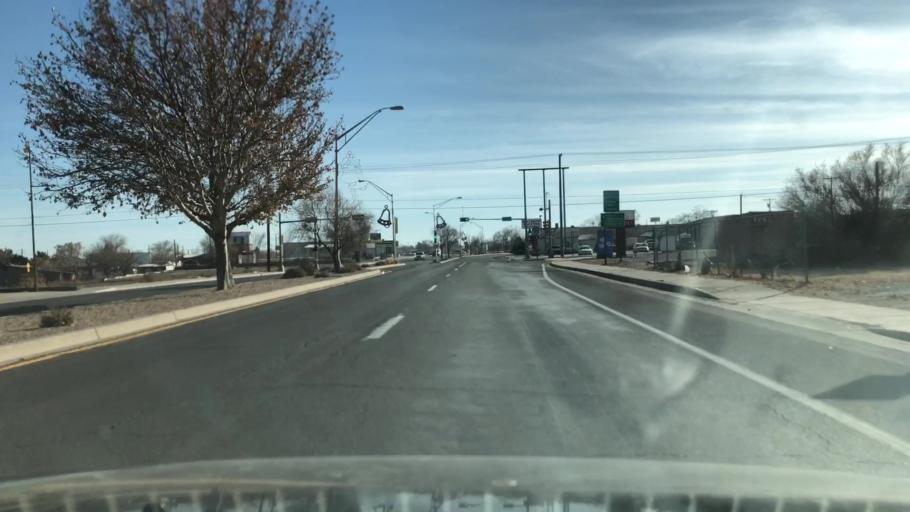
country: US
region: New Mexico
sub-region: Socorro County
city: Socorro
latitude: 34.0544
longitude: -106.8916
